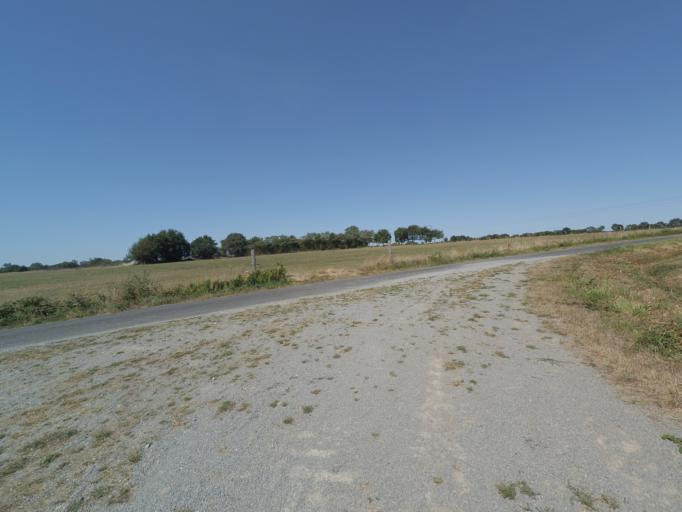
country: FR
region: Pays de la Loire
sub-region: Departement de la Loire-Atlantique
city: La Planche
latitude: 46.9989
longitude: -1.4139
